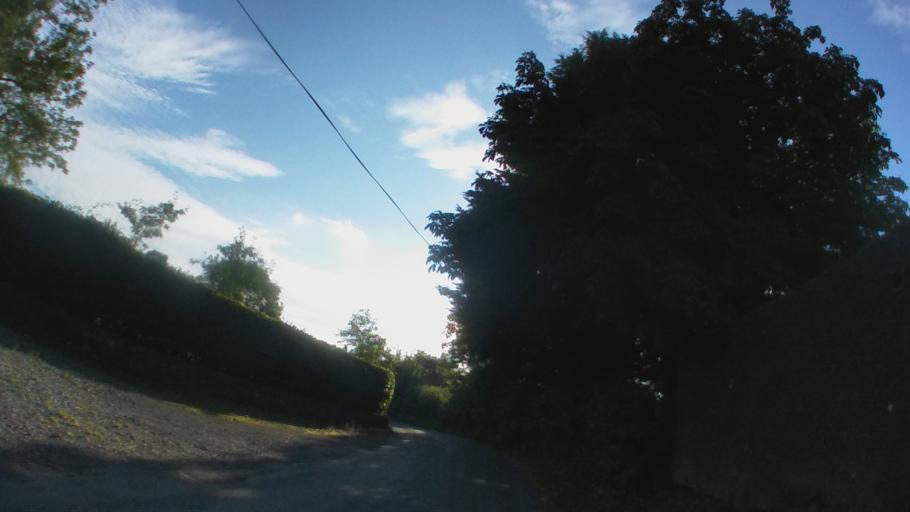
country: IE
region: Leinster
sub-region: Kilkenny
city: Kilkenny
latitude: 52.6976
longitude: -7.2019
